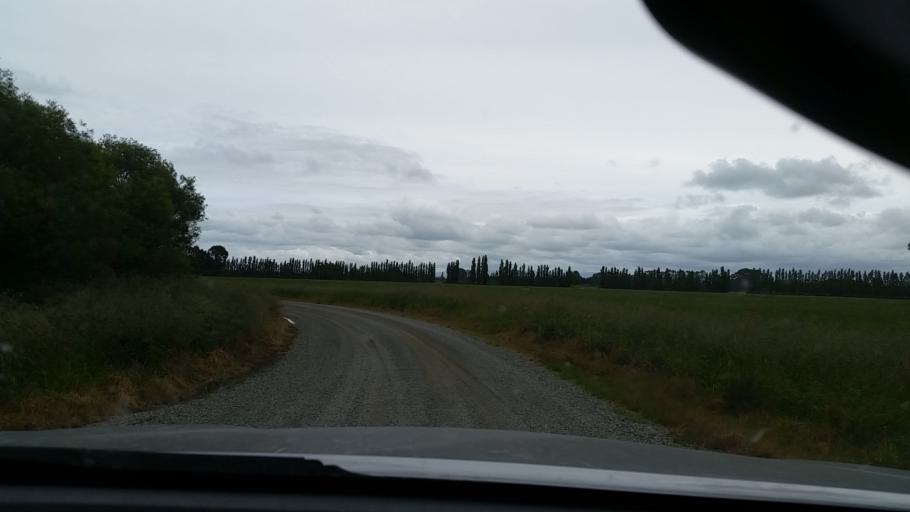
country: NZ
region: Southland
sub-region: Southland District
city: Winton
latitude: -46.1993
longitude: 168.3029
